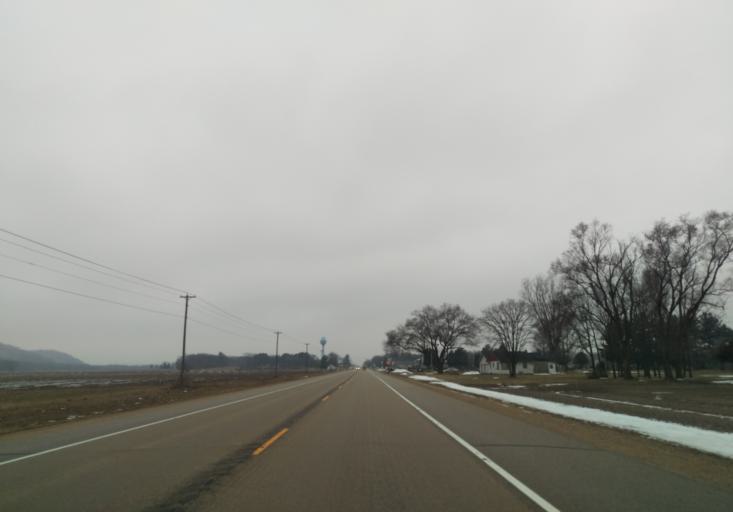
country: US
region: Wisconsin
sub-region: Dane County
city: Mazomanie
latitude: 43.1617
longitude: -89.8941
